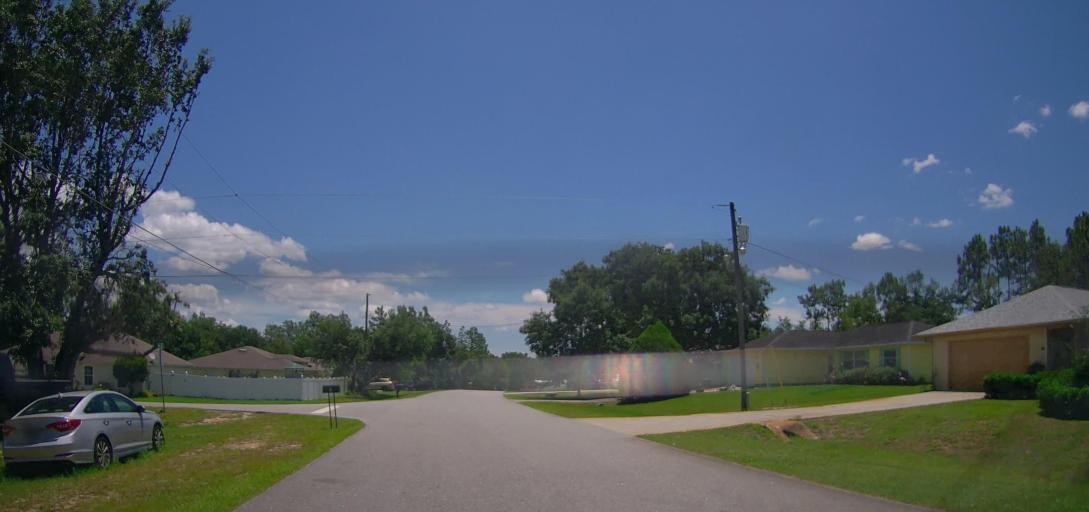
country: US
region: Florida
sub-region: Marion County
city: Silver Springs Shores
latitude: 29.1398
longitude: -82.0259
